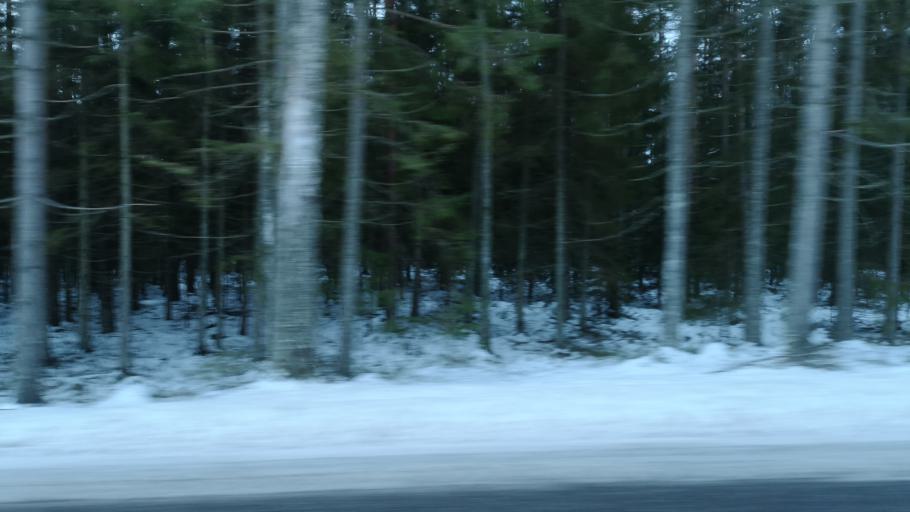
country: FI
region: Uusimaa
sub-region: Helsinki
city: Karjalohja
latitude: 60.2019
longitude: 23.6539
